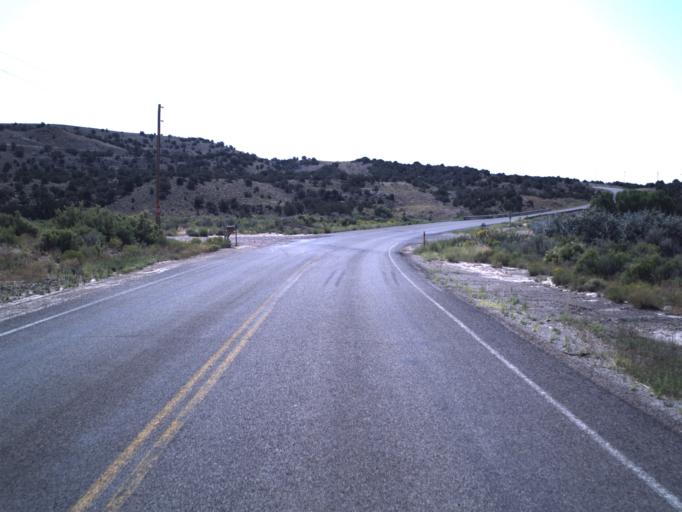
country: US
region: Utah
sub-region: Duchesne County
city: Duchesne
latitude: 40.2599
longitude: -110.4087
